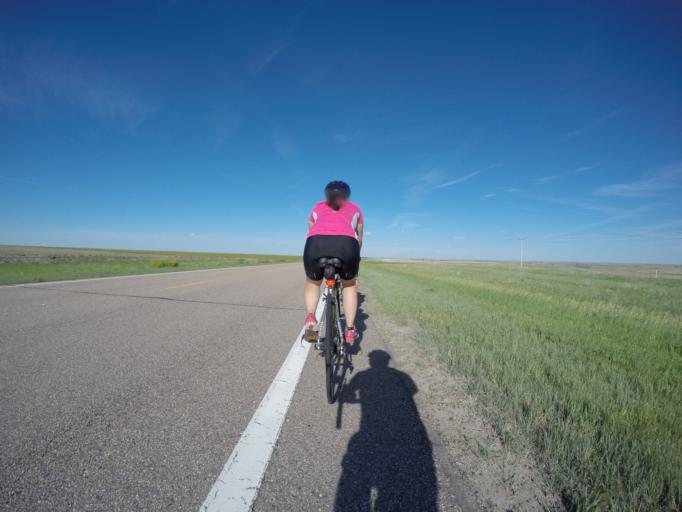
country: US
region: Kansas
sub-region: Cheyenne County
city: Saint Francis
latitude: 39.7568
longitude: -101.9209
